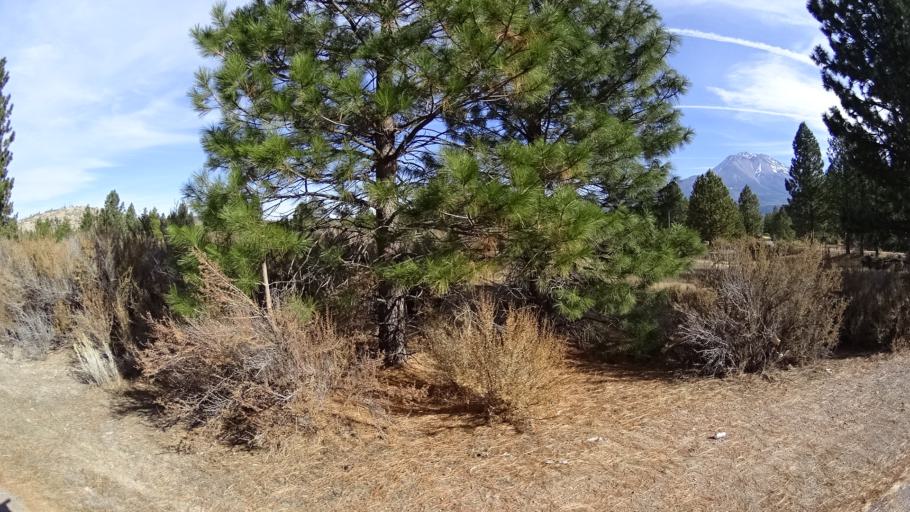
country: US
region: California
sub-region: Siskiyou County
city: Weed
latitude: 41.4225
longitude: -122.3984
